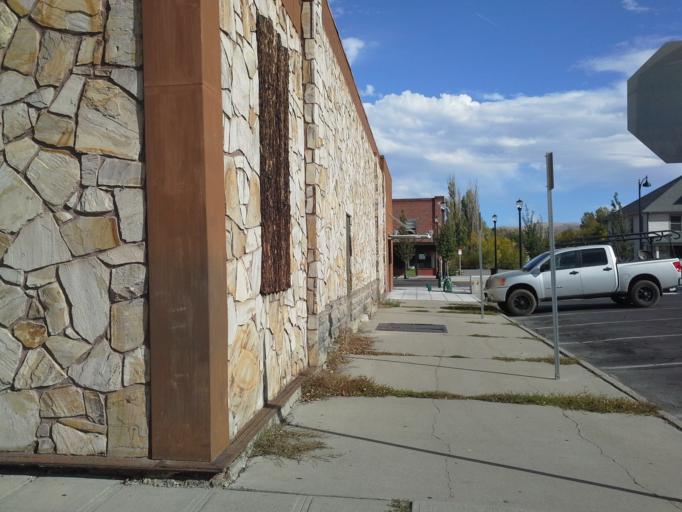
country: US
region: Oregon
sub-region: Baker County
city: Baker City
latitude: 44.7763
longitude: -117.8297
